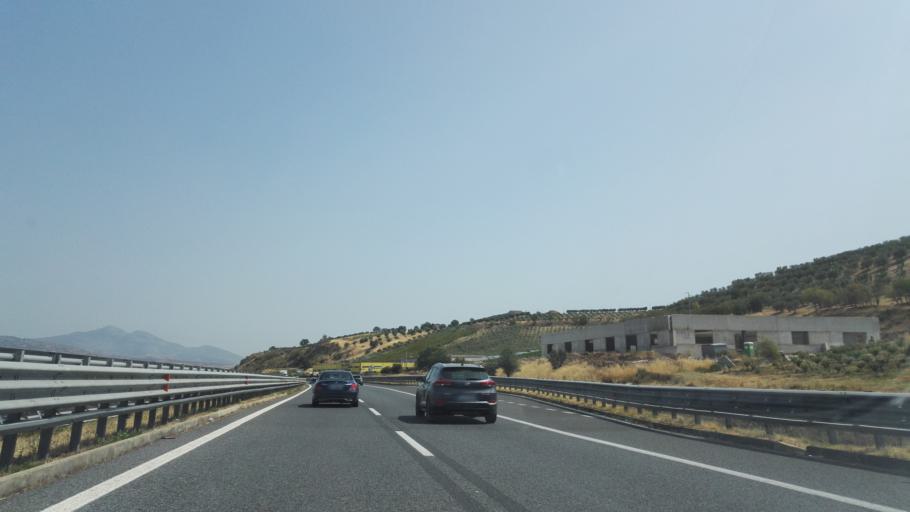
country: IT
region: Calabria
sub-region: Provincia di Cosenza
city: San Lorenzo del Vallo
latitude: 39.6916
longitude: 16.2330
